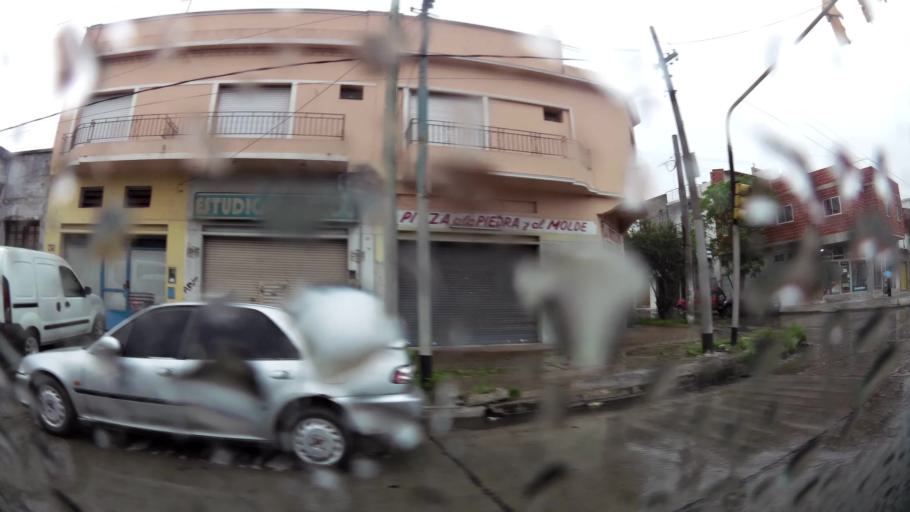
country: AR
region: Buenos Aires
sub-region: Partido de Lanus
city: Lanus
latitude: -34.6992
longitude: -58.4110
